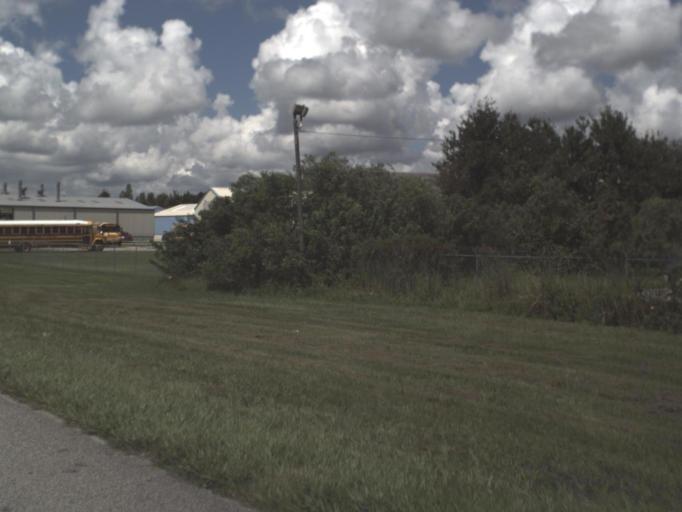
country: US
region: Florida
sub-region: Polk County
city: Polk City
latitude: 28.1503
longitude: -81.8795
